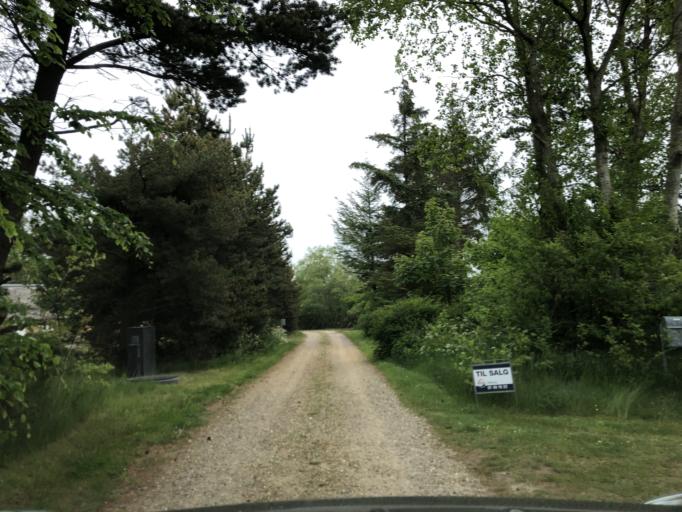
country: DK
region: Central Jutland
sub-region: Holstebro Kommune
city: Ulfborg
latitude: 56.2720
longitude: 8.1637
